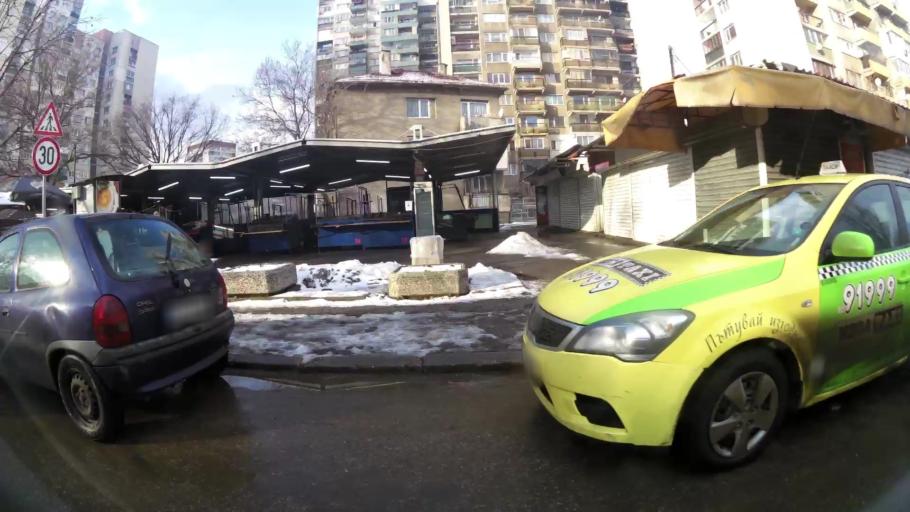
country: BG
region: Sofia-Capital
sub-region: Stolichna Obshtina
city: Sofia
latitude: 42.6970
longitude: 23.2865
